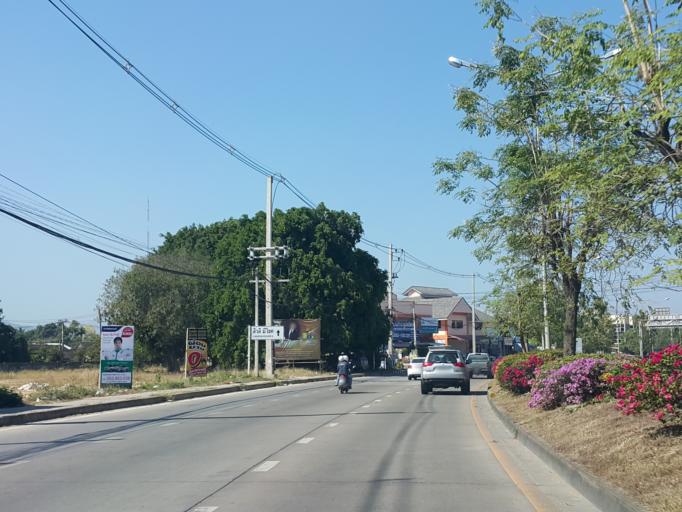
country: TH
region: Chiang Mai
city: Chiang Mai
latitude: 18.8242
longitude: 99.0082
